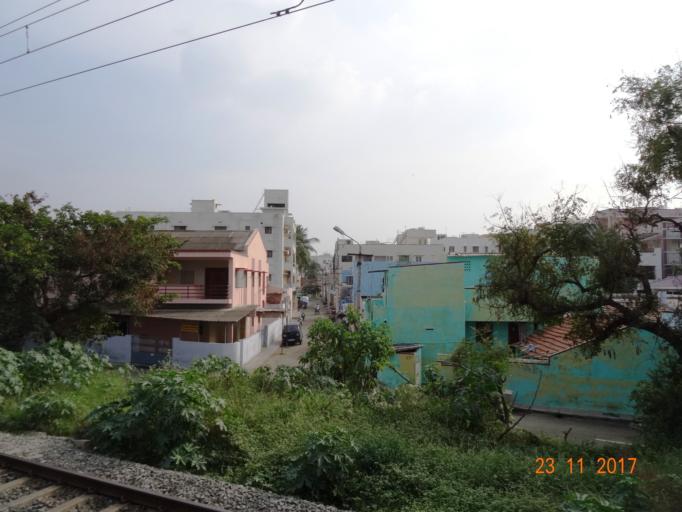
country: IN
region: Tamil Nadu
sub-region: Coimbatore
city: Coimbatore
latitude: 11.0300
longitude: 76.9691
